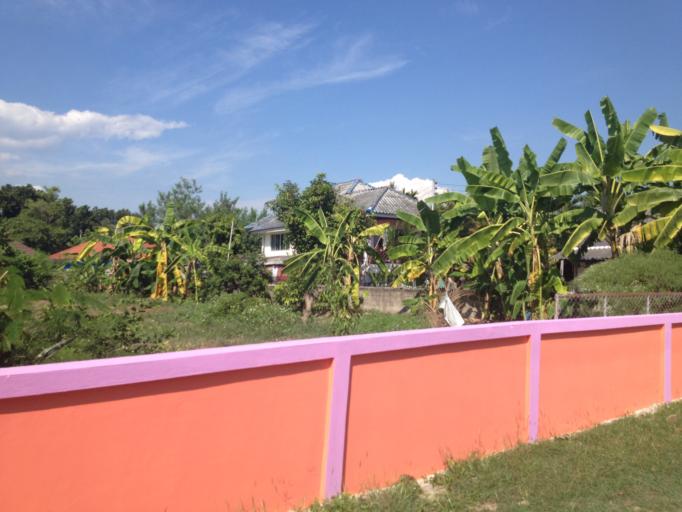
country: TH
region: Chiang Mai
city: Hang Dong
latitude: 18.6948
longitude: 98.9352
